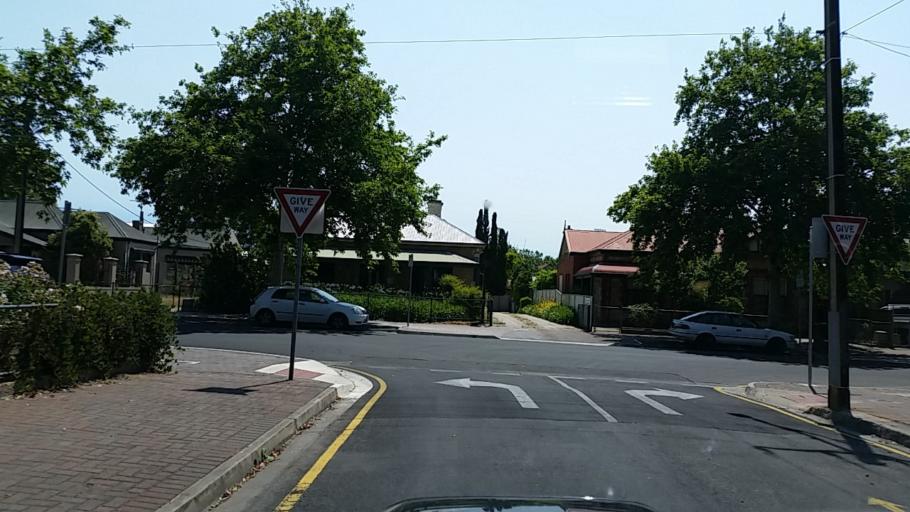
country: AU
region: South Australia
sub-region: Norwood Payneham St Peters
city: Trinity Gardens
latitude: -34.9197
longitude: 138.6346
